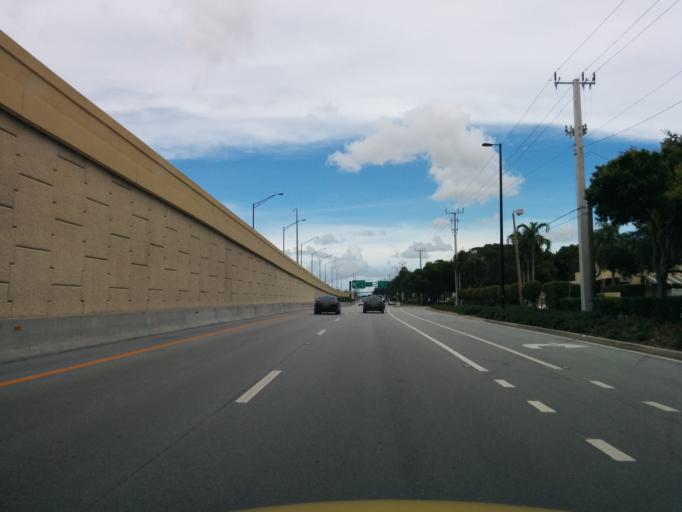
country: US
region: Florida
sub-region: Broward County
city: Pine Island Ridge
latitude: 26.1035
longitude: -80.2706
